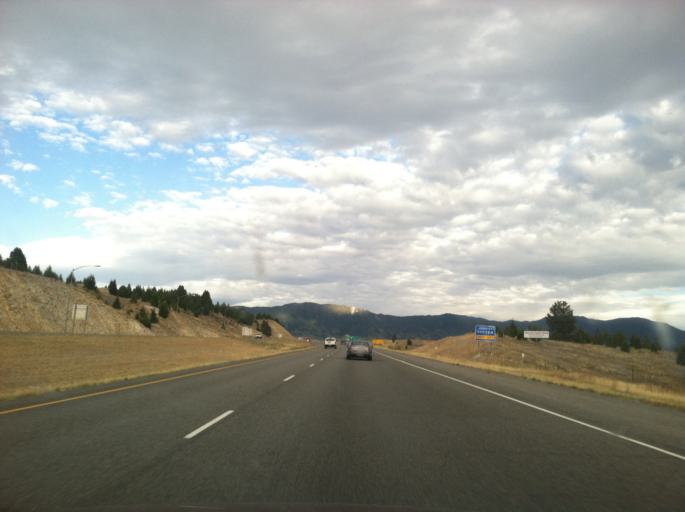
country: US
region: Montana
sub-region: Silver Bow County
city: Butte
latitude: 46.0055
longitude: -112.5863
